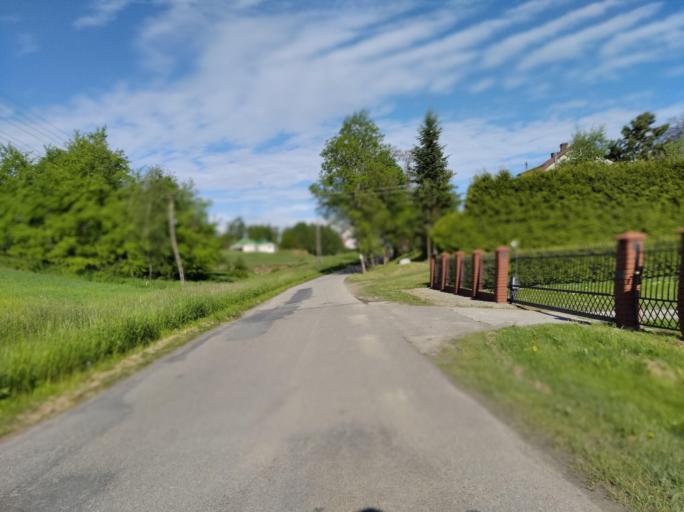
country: PL
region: Subcarpathian Voivodeship
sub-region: Powiat strzyzowski
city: Frysztak
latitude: 49.8467
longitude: 21.5348
